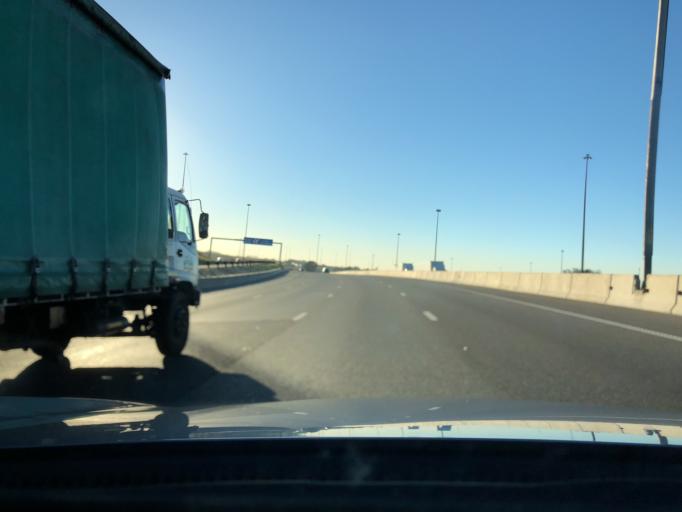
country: ZA
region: Gauteng
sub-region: Ekurhuleni Metropolitan Municipality
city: Germiston
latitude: -26.2483
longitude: 28.1413
